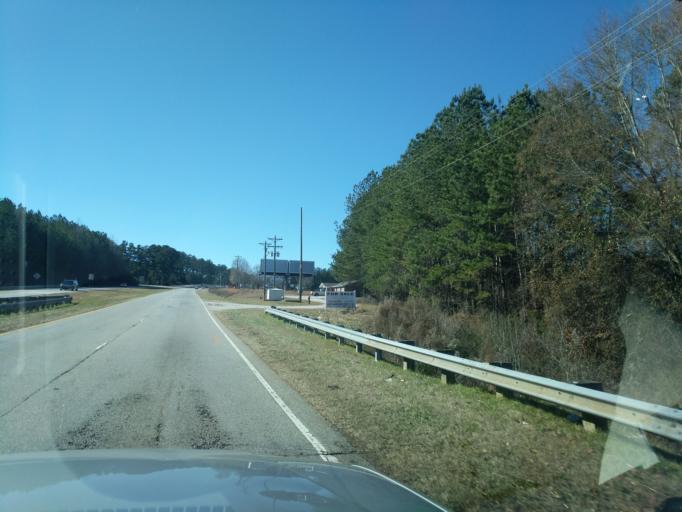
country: US
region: South Carolina
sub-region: Oconee County
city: Westminster
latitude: 34.6683
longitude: -83.0270
